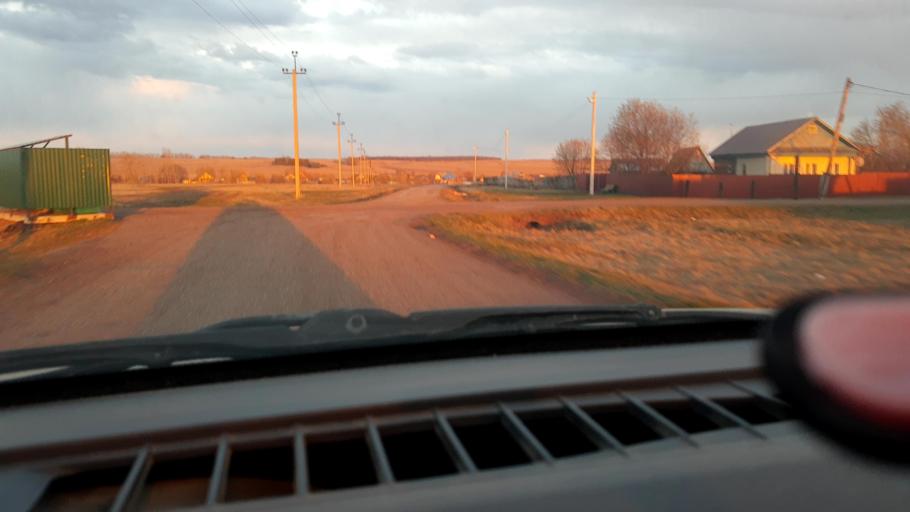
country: RU
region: Bashkortostan
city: Asanovo
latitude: 54.9092
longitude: 55.4925
